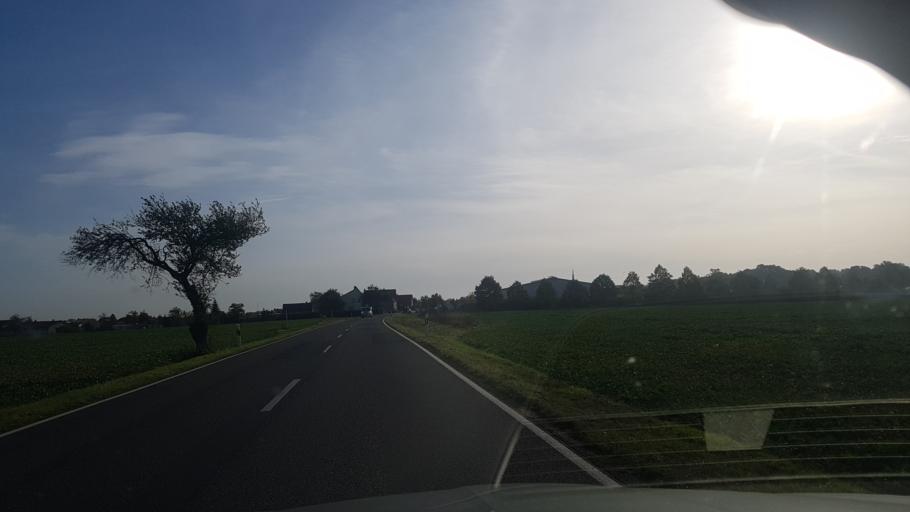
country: DE
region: Brandenburg
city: Grossthiemig
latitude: 51.3860
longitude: 13.6634
